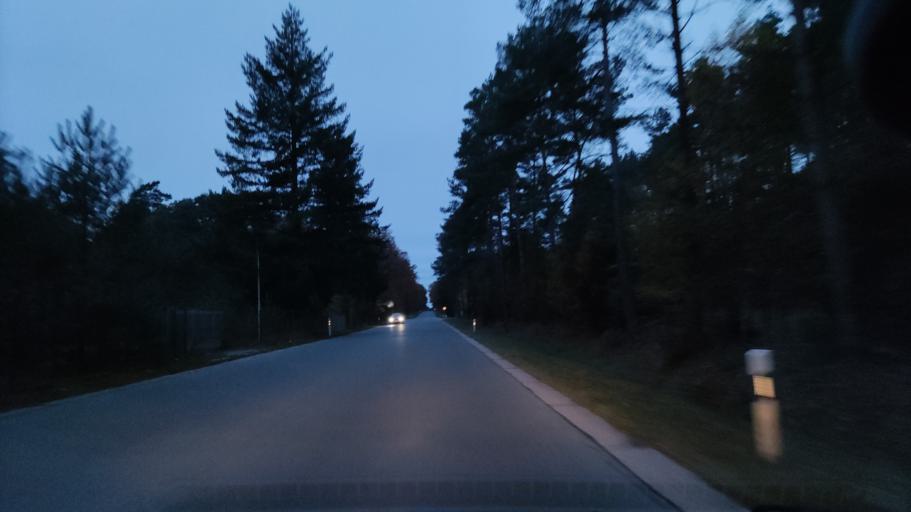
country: DE
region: Lower Saxony
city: Munster
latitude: 53.0060
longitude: 10.1125
